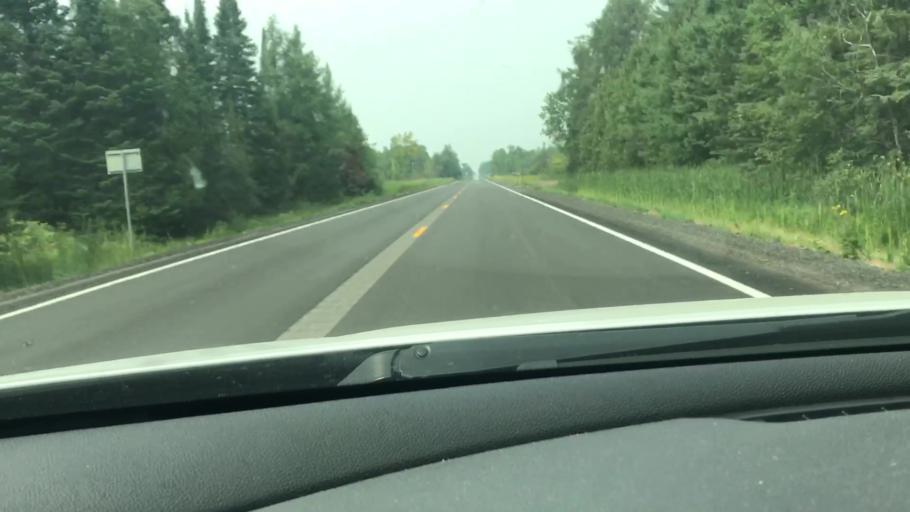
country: US
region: Minnesota
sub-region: Itasca County
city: Cohasset
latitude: 47.3514
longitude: -93.8402
